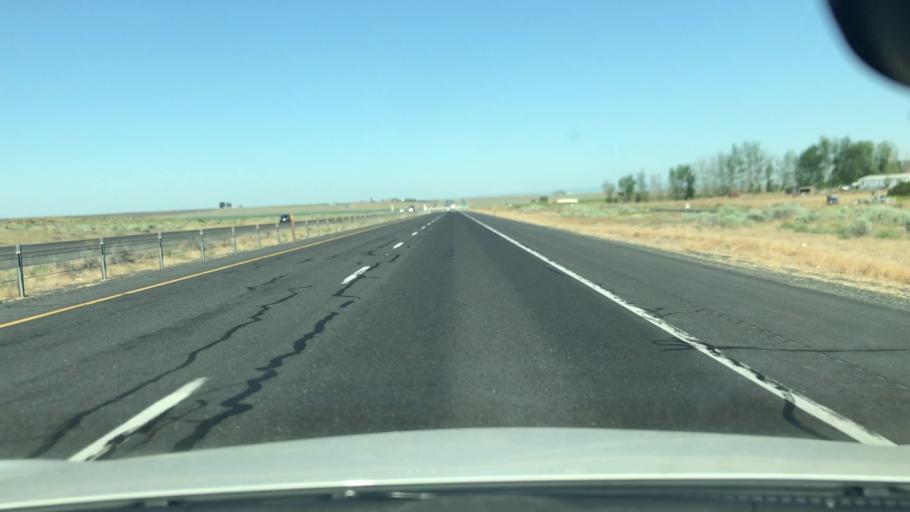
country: US
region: Washington
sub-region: Grant County
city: Cascade Valley
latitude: 47.1042
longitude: -119.4311
